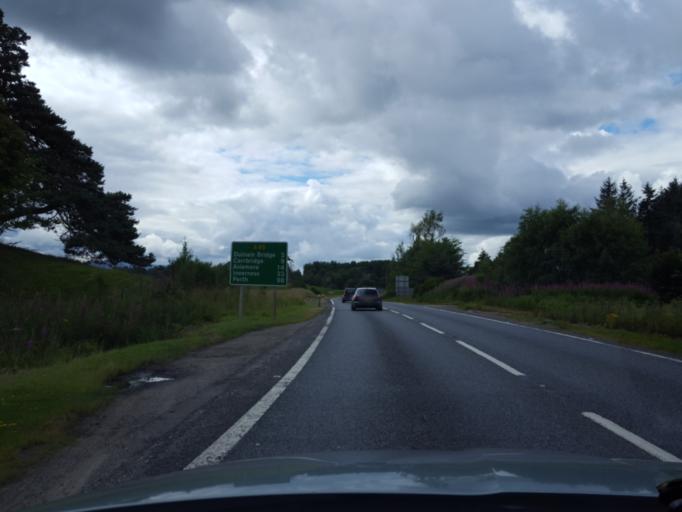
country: GB
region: Scotland
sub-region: Highland
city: Grantown on Spey
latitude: 57.3192
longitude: -3.6200
